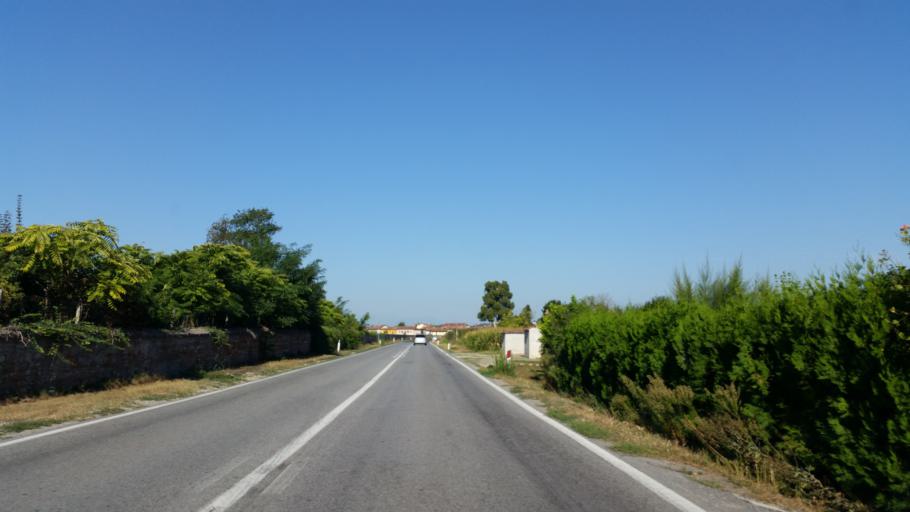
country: IT
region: Piedmont
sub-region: Provincia di Cuneo
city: Cinzano
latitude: 44.6837
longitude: 7.9037
